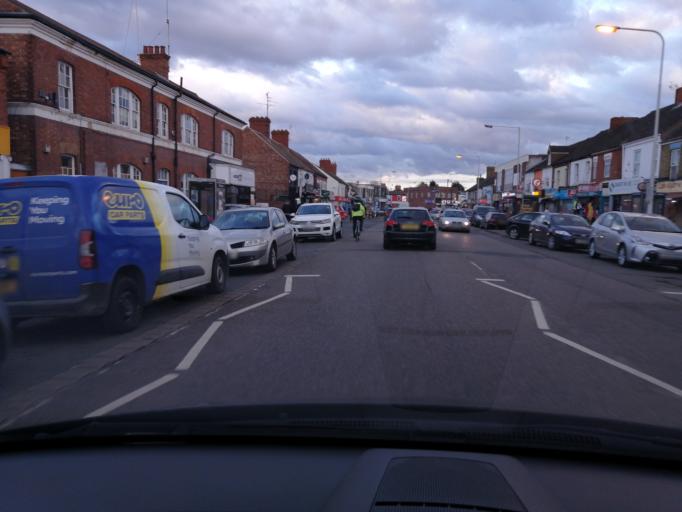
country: GB
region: England
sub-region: Peterborough
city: Peterborough
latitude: 52.5886
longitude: -0.2482
